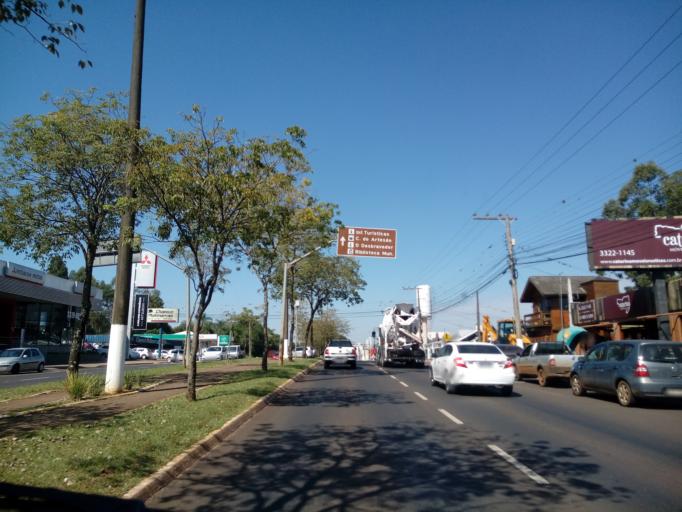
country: BR
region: Santa Catarina
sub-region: Chapeco
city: Chapeco
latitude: -27.0825
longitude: -52.6205
